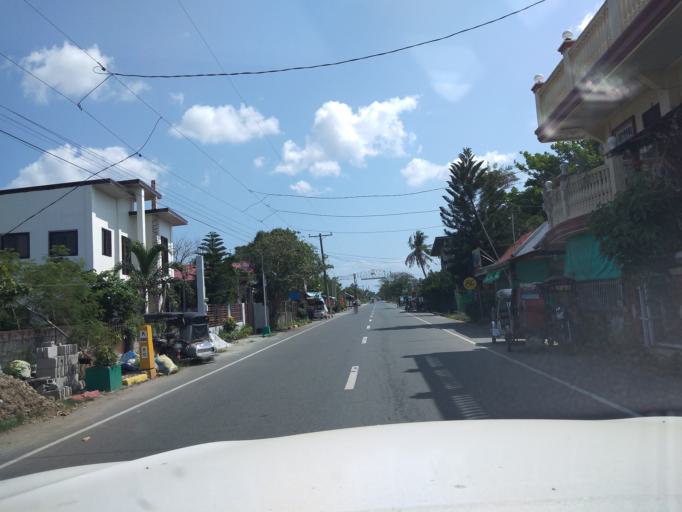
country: PH
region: Central Luzon
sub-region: Province of Pampanga
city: Bahay Pare
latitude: 15.0443
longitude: 120.8788
